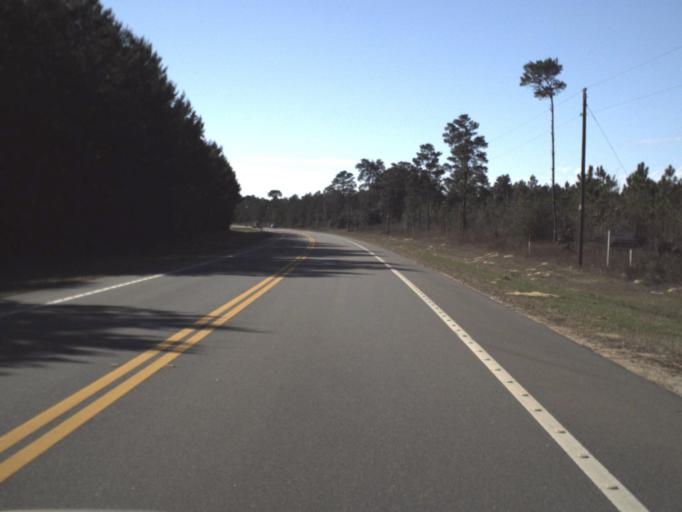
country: US
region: Florida
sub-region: Bay County
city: Youngstown
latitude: 30.4362
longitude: -85.3381
